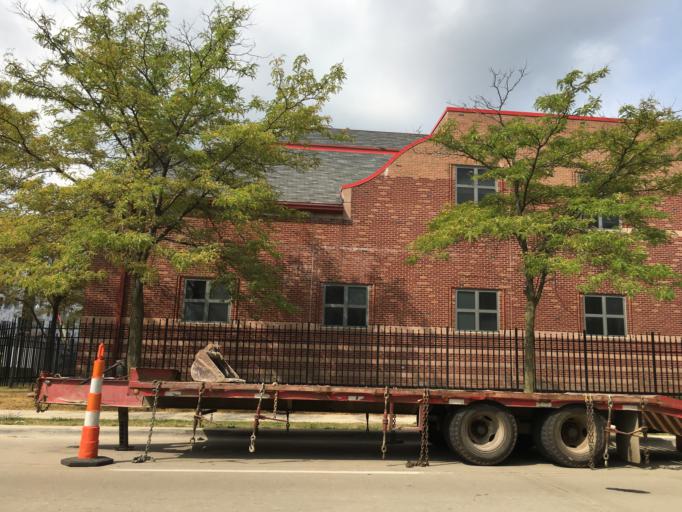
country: US
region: Michigan
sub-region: Wayne County
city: Detroit
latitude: 42.3467
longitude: -83.0548
